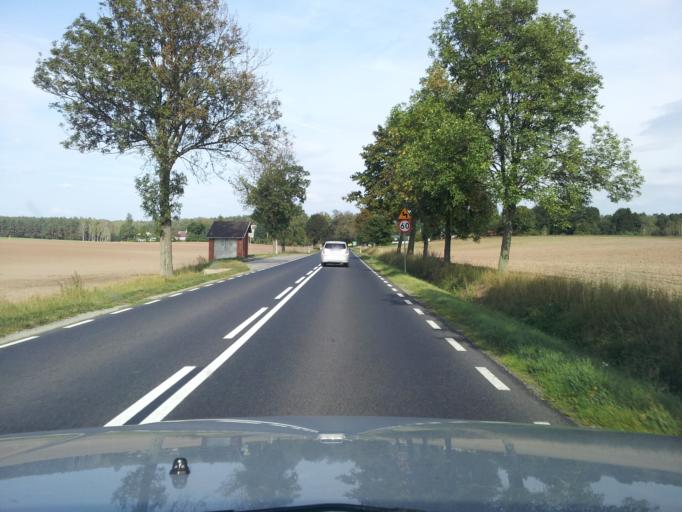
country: PL
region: Warmian-Masurian Voivodeship
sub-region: Powiat ilawski
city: Lubawa
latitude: 53.5809
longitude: 19.8069
